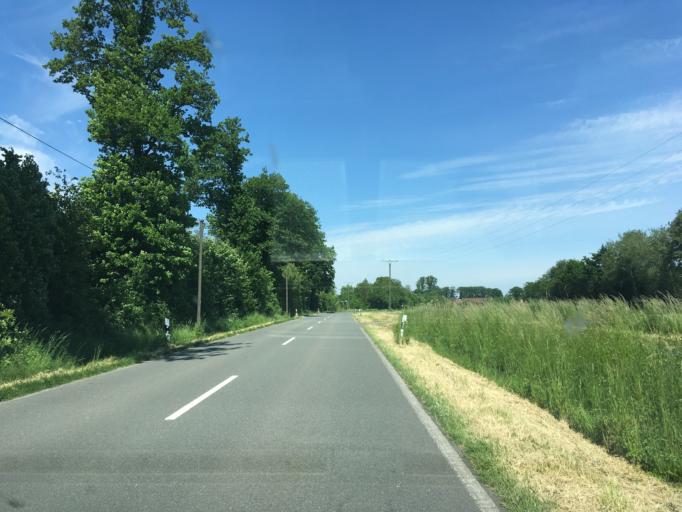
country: DE
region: North Rhine-Westphalia
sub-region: Regierungsbezirk Munster
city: Borken
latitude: 51.8738
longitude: 6.8292
